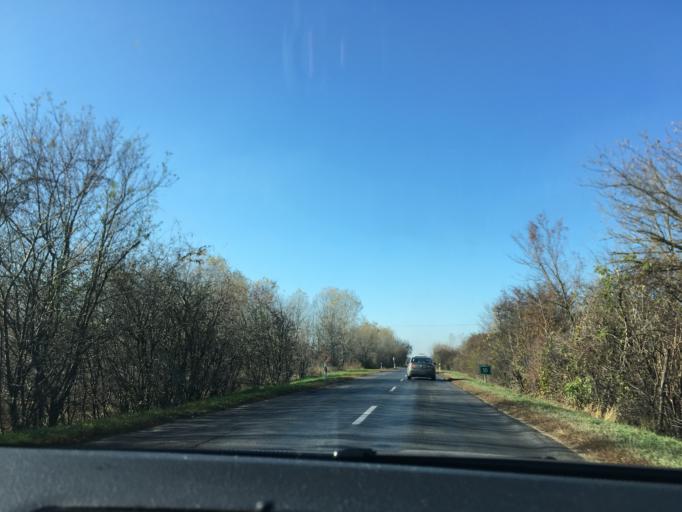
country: HU
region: Hajdu-Bihar
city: Hajdusamson
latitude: 47.5254
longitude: 21.7714
